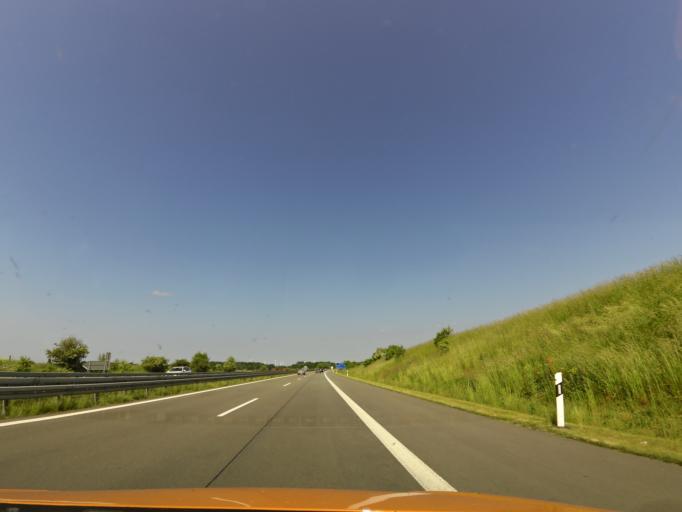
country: DE
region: Brandenburg
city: Gerdshagen
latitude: 53.2346
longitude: 12.2002
